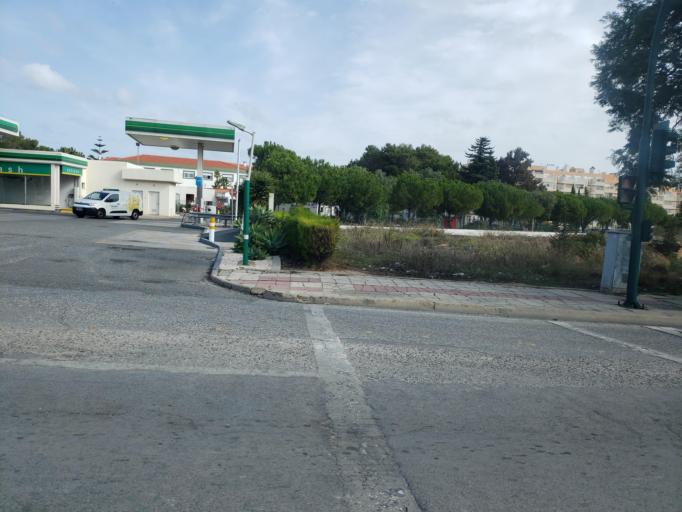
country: PT
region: Faro
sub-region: Portimao
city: Portimao
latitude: 37.1435
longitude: -8.5483
